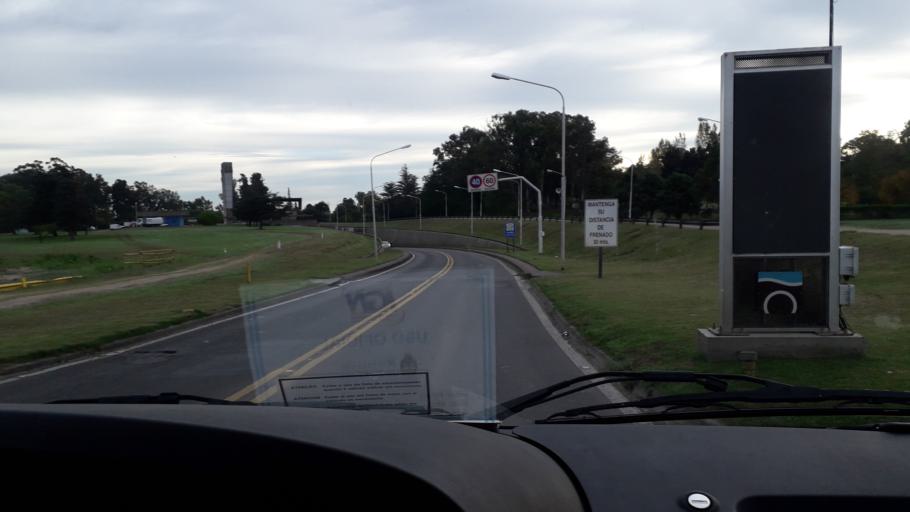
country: AR
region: Entre Rios
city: Parana
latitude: -31.7153
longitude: -60.5017
